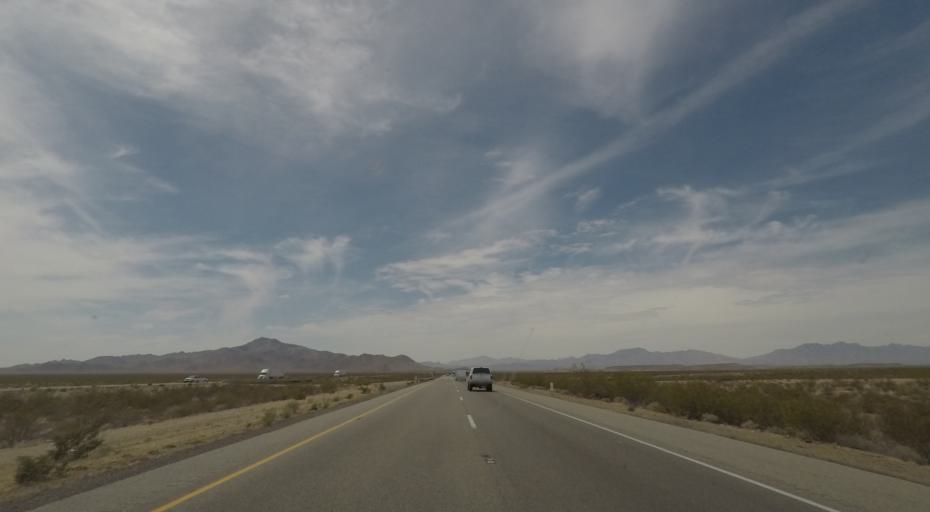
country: US
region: California
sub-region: San Bernardino County
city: Needles
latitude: 34.8067
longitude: -115.2541
